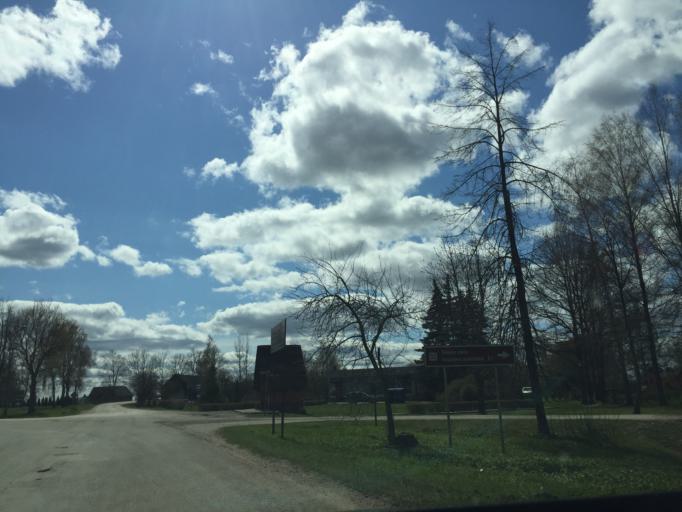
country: LV
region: Vilanu
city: Vilani
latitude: 56.7342
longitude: 27.0670
